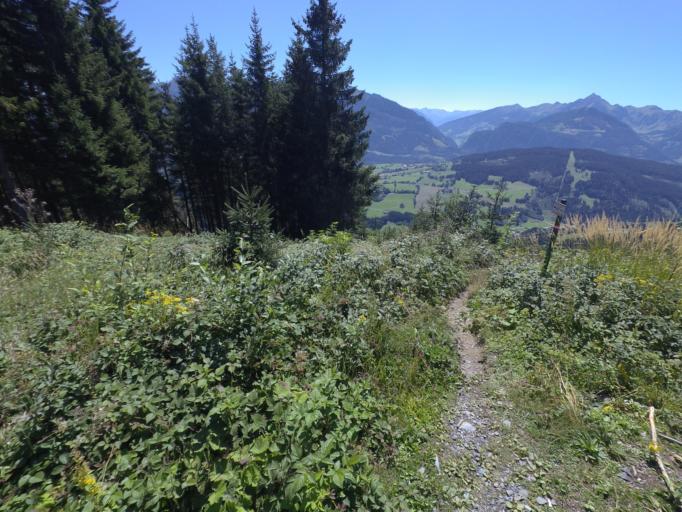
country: AT
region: Salzburg
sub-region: Politischer Bezirk Sankt Johann im Pongau
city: Goldegg
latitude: 47.3366
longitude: 13.0683
